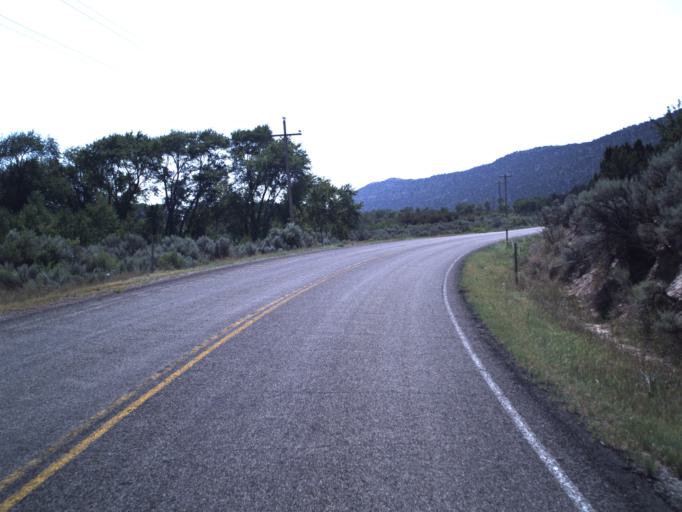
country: US
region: Utah
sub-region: Duchesne County
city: Duchesne
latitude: 40.2926
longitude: -110.5043
